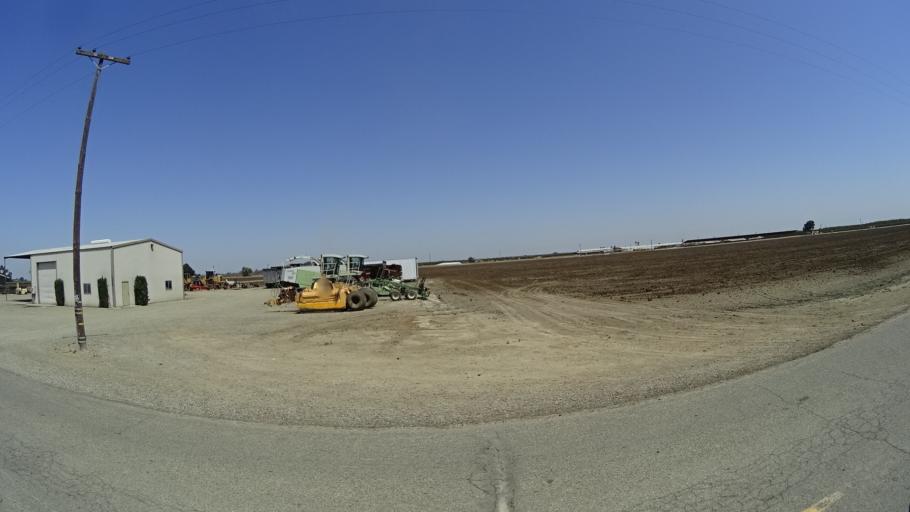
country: US
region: California
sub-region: Kings County
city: Armona
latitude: 36.3717
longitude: -119.7502
